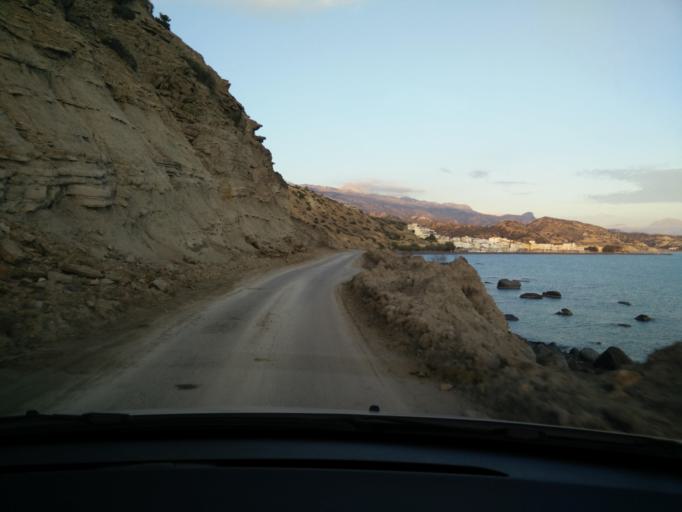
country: GR
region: Crete
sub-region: Nomos Lasithiou
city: Gra Liyia
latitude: 35.0000
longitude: 25.5769
